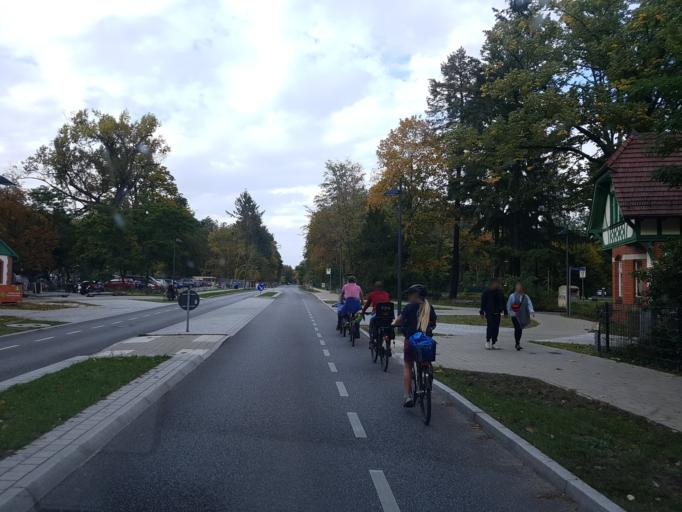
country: DE
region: Brandenburg
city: Fichtenwalde
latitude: 52.2650
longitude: 12.9220
